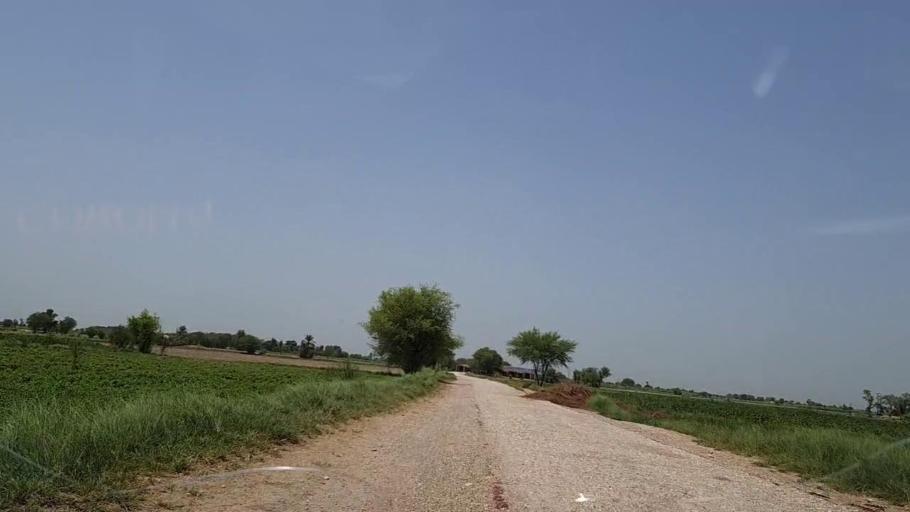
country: PK
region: Sindh
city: Tharu Shah
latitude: 26.9208
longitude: 68.0579
